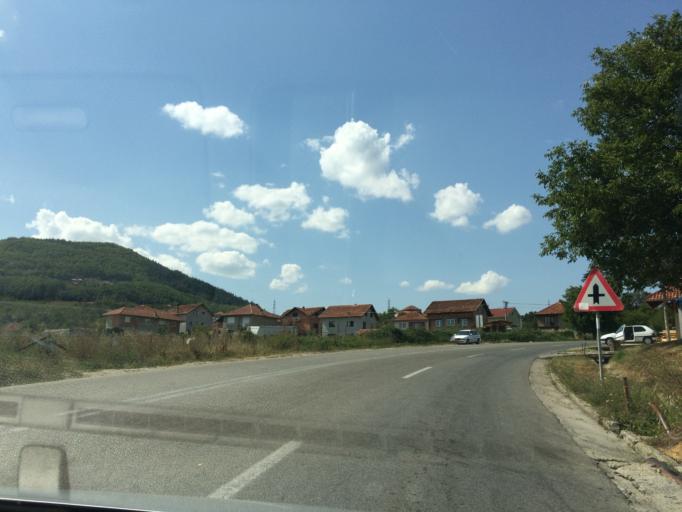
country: RS
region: Central Serbia
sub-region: Zlatiborski Okrug
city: Prijepolje
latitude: 43.3605
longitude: 19.6272
